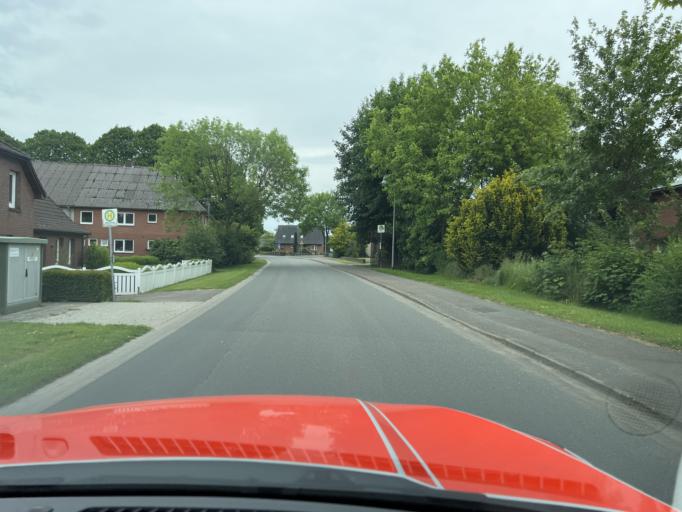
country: DE
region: Schleswig-Holstein
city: Hemmingstedt
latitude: 54.1562
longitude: 9.0922
